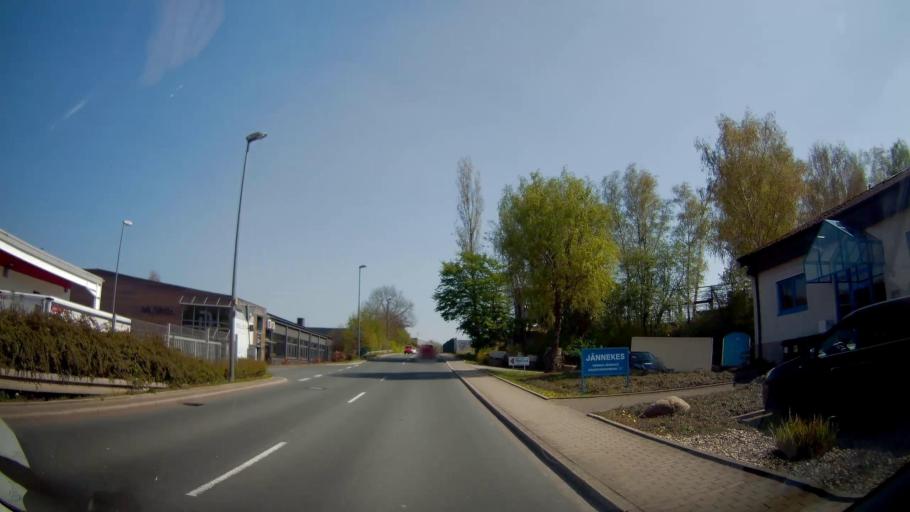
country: DE
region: North Rhine-Westphalia
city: Bochum-Hordel
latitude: 51.4889
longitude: 7.1610
